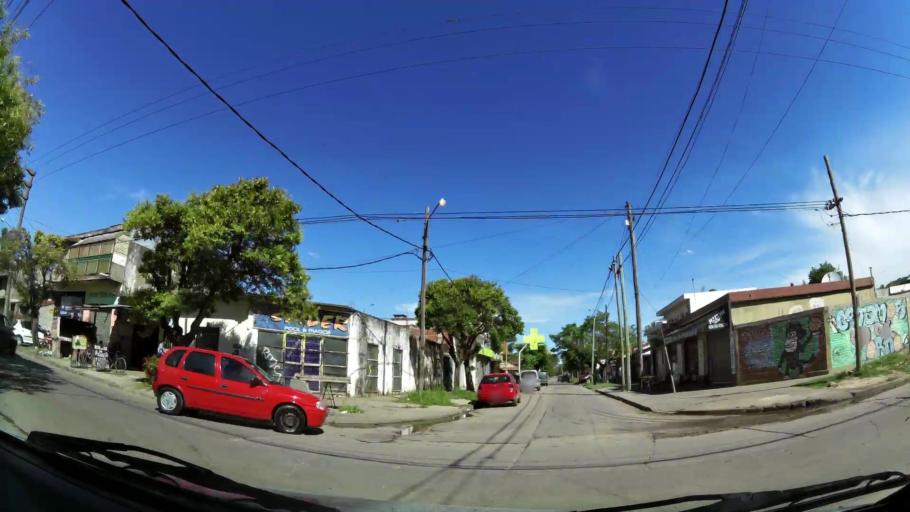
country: AR
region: Buenos Aires
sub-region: Partido de Almirante Brown
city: Adrogue
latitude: -34.7987
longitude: -58.3596
